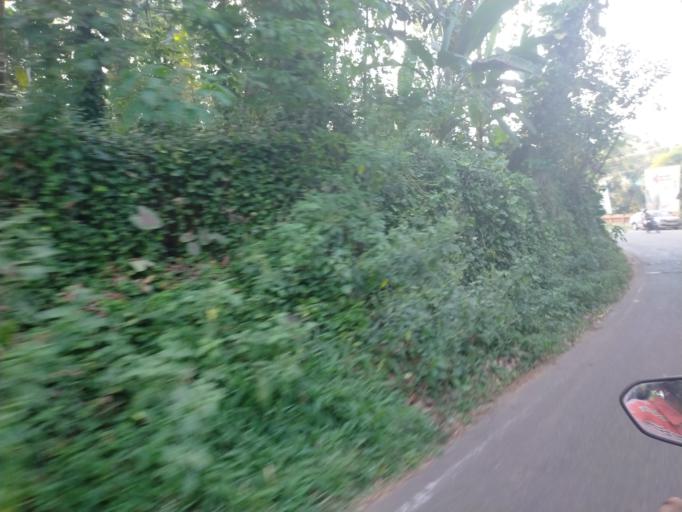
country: IN
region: Kerala
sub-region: Kottayam
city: Vaikam
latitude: 9.7543
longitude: 76.5042
